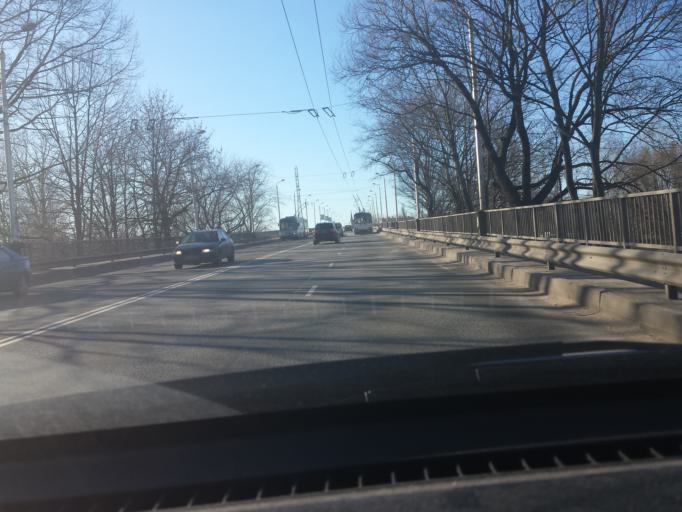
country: LV
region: Riga
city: Riga
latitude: 56.9519
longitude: 24.1654
